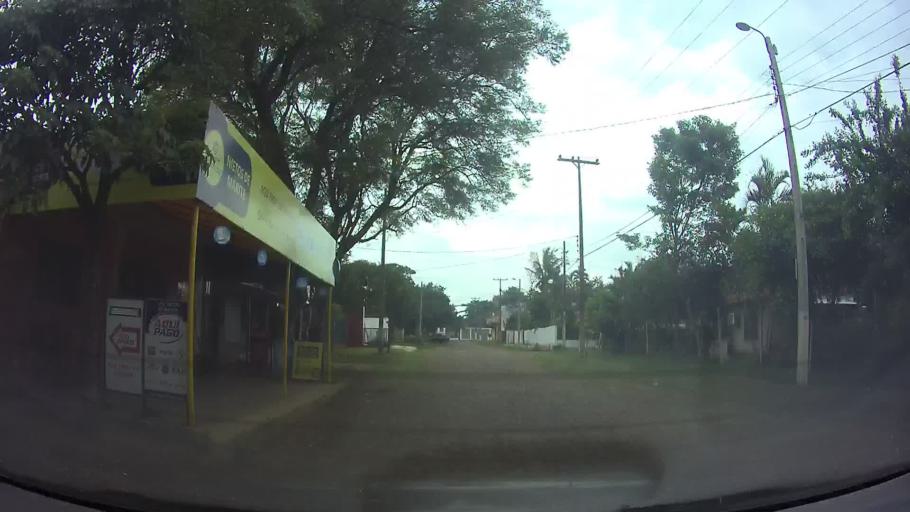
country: PY
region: Central
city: San Lorenzo
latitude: -25.2658
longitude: -57.4789
